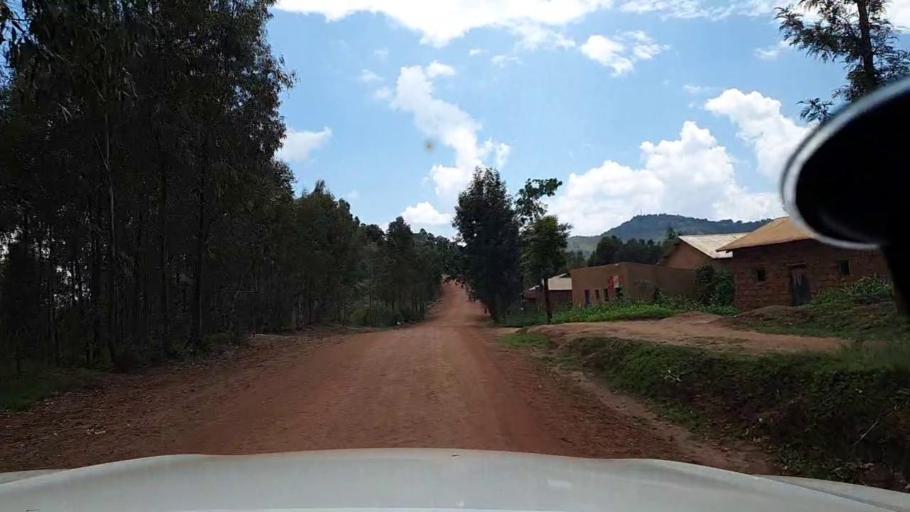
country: RW
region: Kigali
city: Kigali
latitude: -1.7624
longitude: 29.8417
